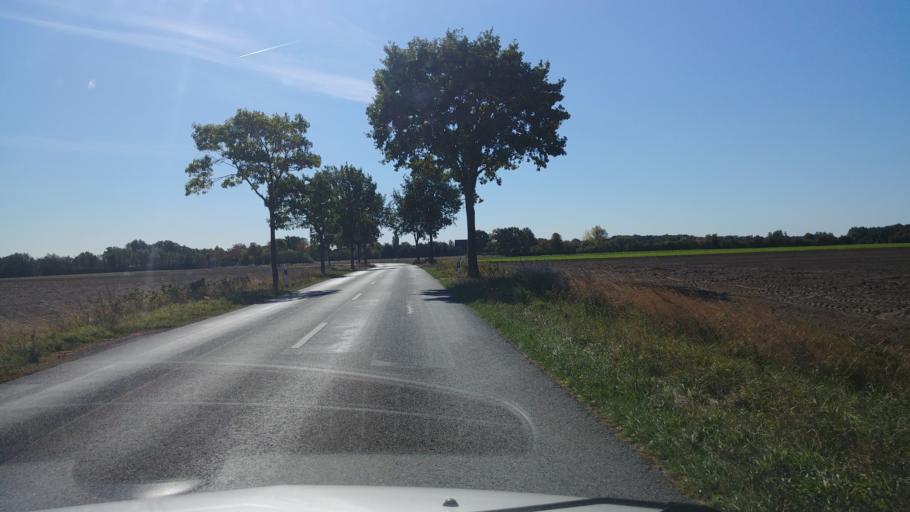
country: DE
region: Lower Saxony
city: Hillerse
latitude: 52.4022
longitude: 10.4213
